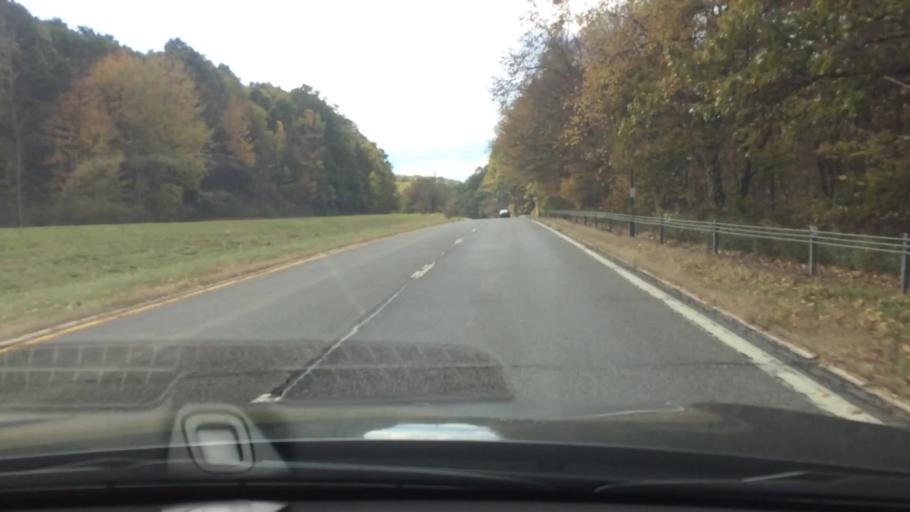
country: US
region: New York
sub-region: Dutchess County
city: Pine Plains
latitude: 41.9438
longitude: -73.7532
